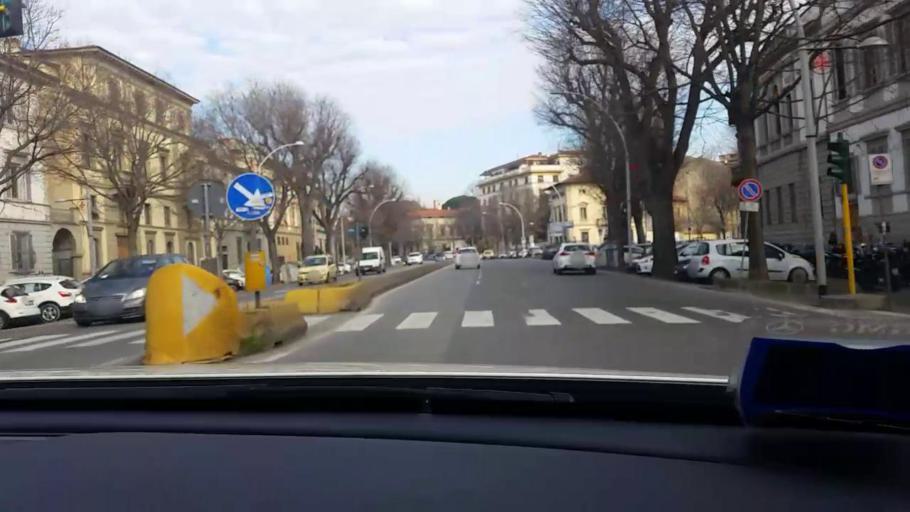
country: IT
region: Tuscany
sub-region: Province of Florence
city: Florence
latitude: 43.7724
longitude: 11.2711
